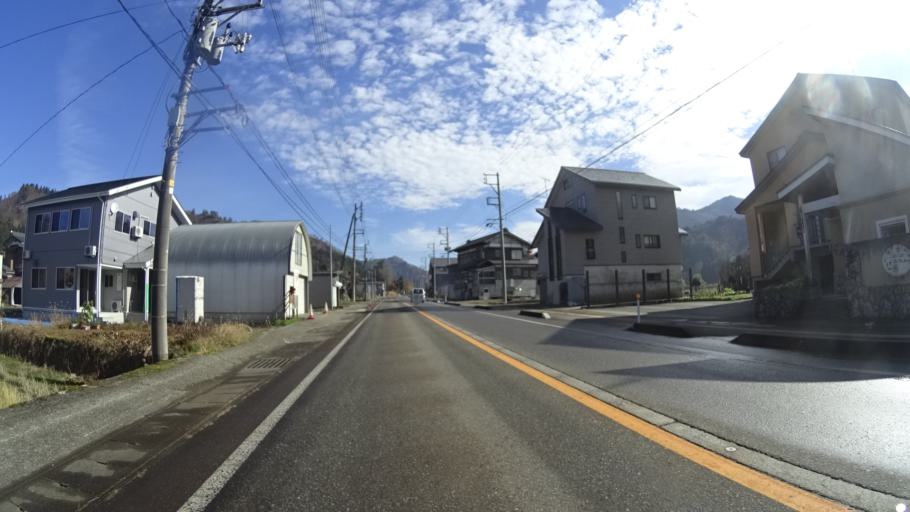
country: JP
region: Niigata
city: Muikamachi
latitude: 37.2268
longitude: 139.0033
